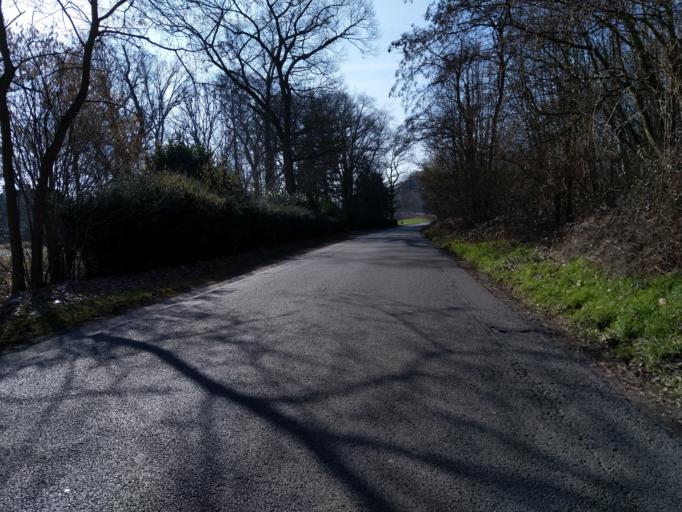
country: BE
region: Wallonia
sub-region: Province du Hainaut
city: Mons
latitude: 50.4916
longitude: 3.9522
